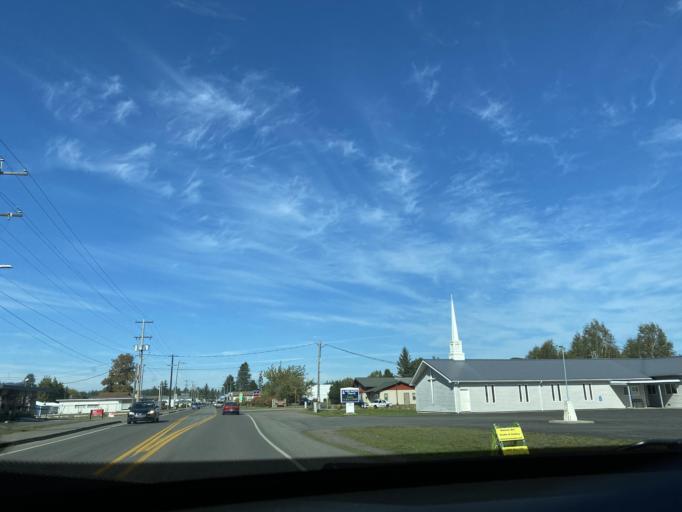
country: US
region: Washington
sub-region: Clallam County
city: Forks
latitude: 47.9440
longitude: -124.3855
